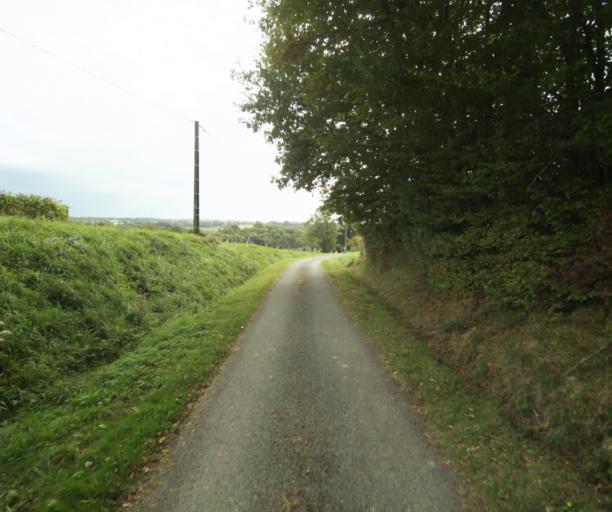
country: FR
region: Midi-Pyrenees
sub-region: Departement du Gers
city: Eauze
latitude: 43.9048
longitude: 0.0905
